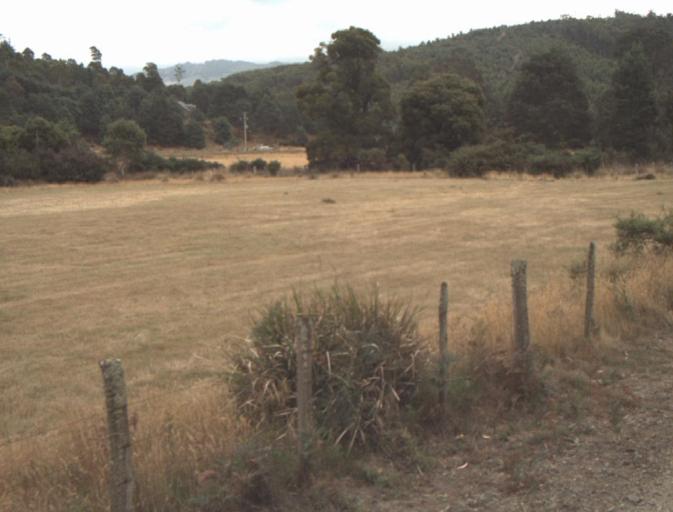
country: AU
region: Tasmania
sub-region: Northern Midlands
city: Evandale
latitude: -41.4629
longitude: 147.4957
